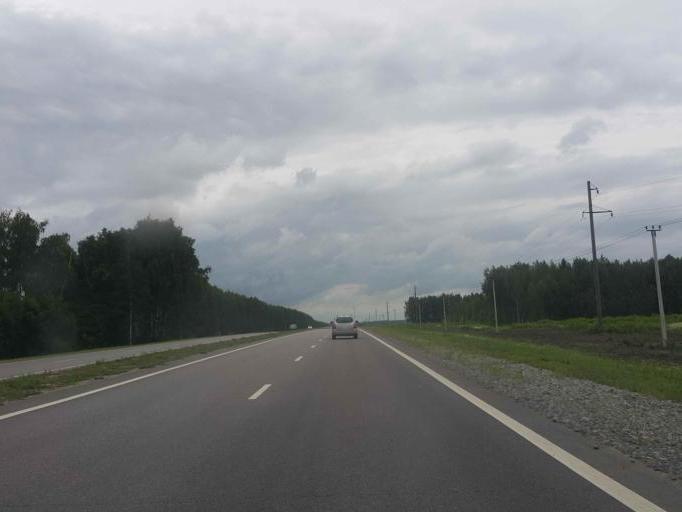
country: RU
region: Tambov
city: Zavoronezhskoye
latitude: 52.8840
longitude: 40.7234
